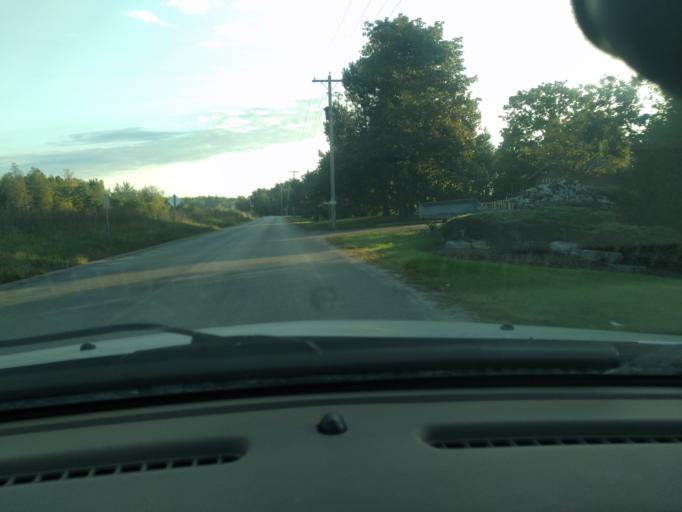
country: CA
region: Ontario
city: Bradford West Gwillimbury
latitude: 44.0448
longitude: -79.6229
